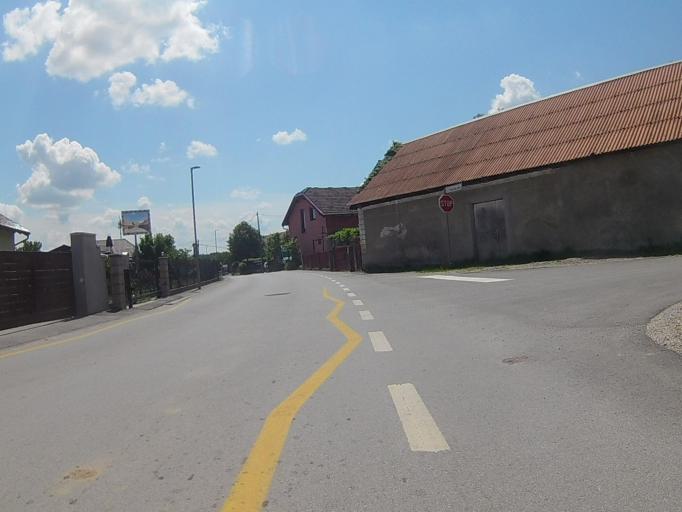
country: SI
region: Hoce-Slivnica
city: Rogoza
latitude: 46.4882
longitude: 15.6938
